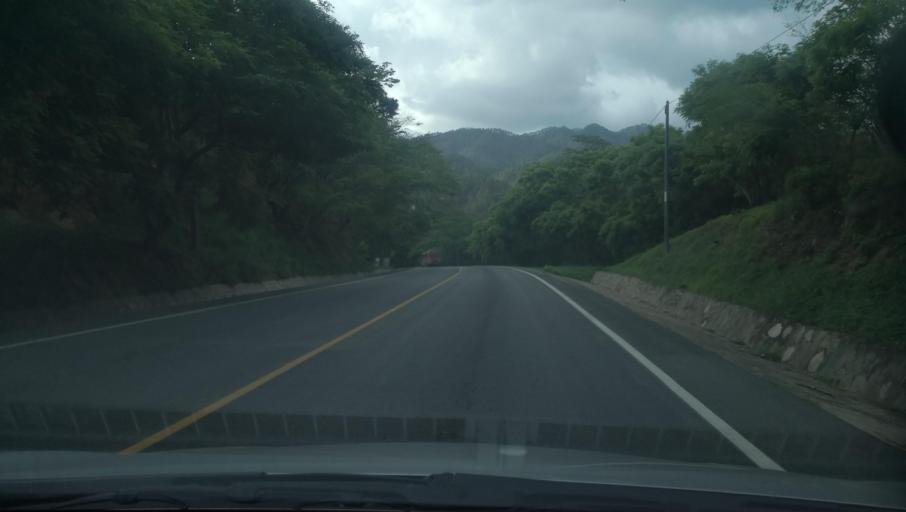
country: NI
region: Nueva Segovia
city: Mozonte
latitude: 13.6895
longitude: -86.4876
